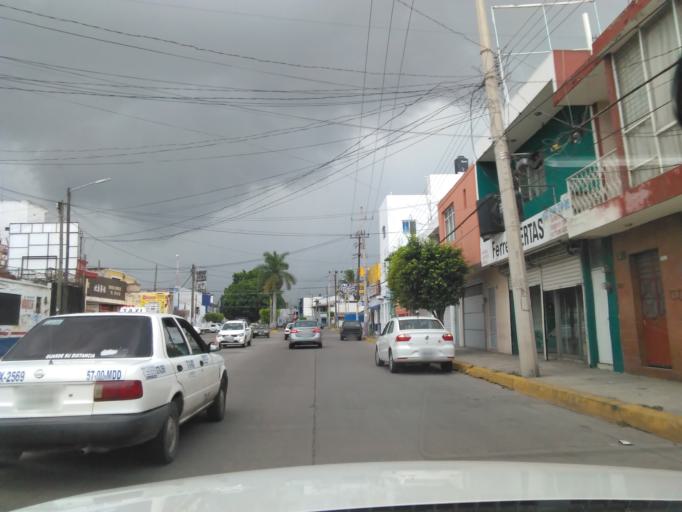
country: MX
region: Nayarit
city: Tepic
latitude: 21.5063
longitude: -104.8885
